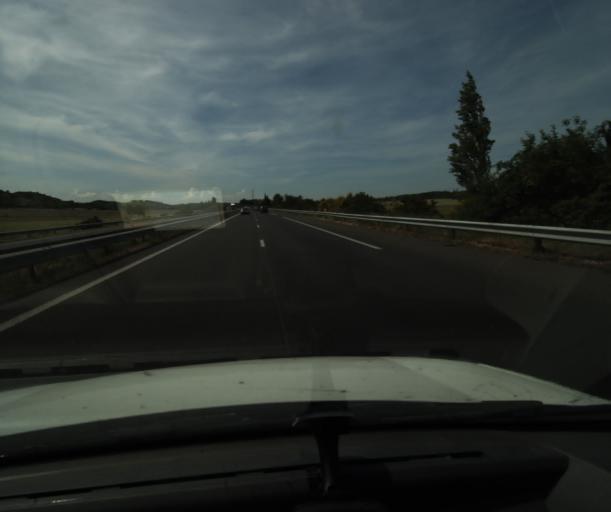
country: FR
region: Languedoc-Roussillon
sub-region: Departement de l'Aude
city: Villeneuve-la-Comptal
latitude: 43.3171
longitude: 1.8792
